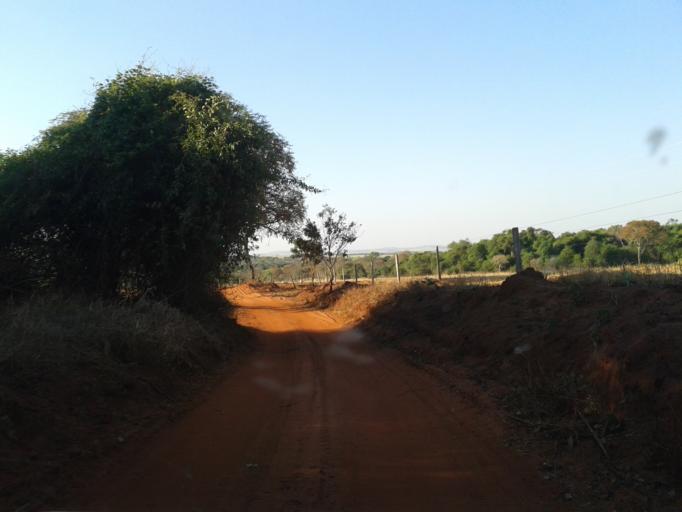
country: BR
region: Minas Gerais
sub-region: Campina Verde
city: Campina Verde
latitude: -19.2510
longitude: -49.5780
